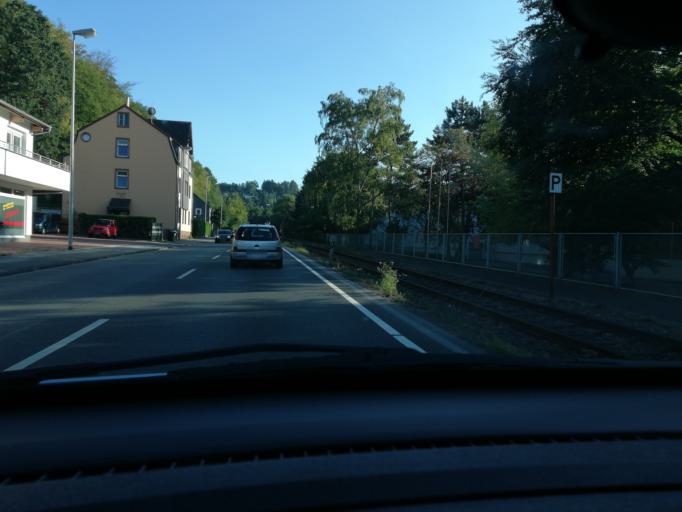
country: DE
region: North Rhine-Westphalia
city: Gevelsberg
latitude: 51.3141
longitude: 7.3412
